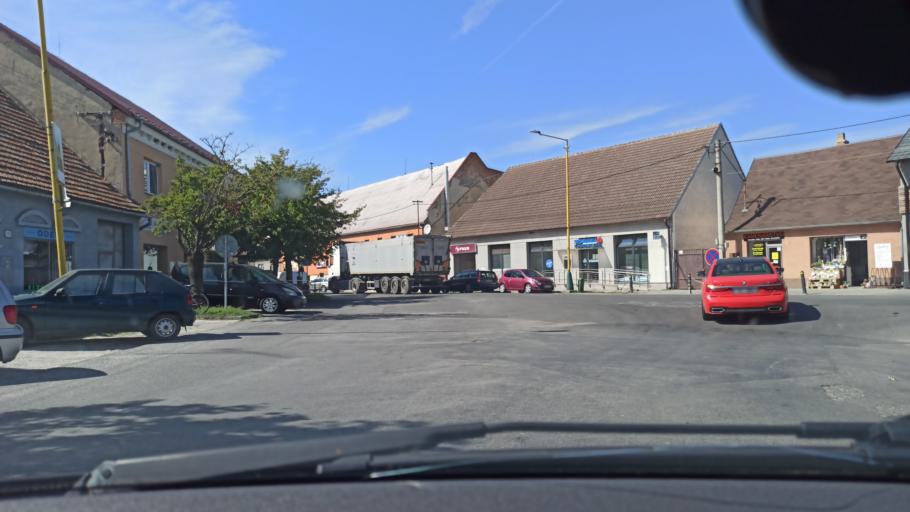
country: SK
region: Trnavsky
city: Gbely
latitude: 48.6370
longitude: 17.1532
